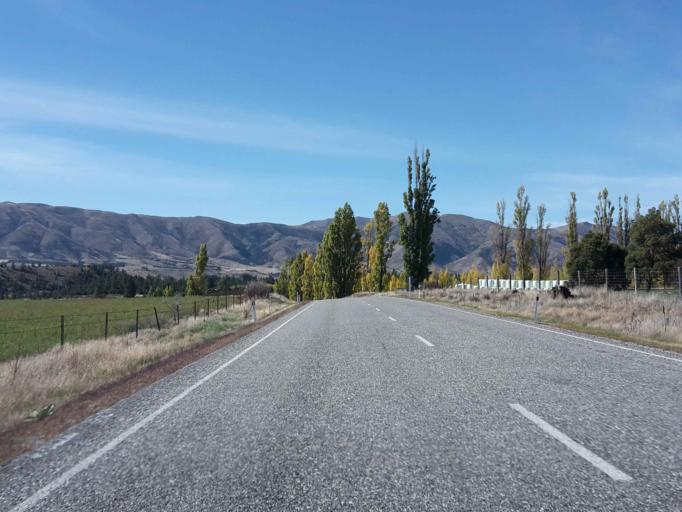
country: NZ
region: Otago
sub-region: Queenstown-Lakes District
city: Wanaka
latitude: -44.7343
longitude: 169.2663
